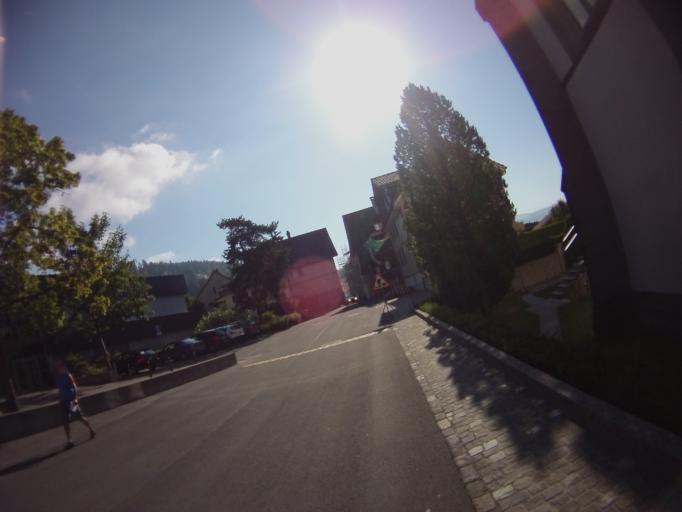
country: CH
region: Zug
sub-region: Zug
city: Unterageri
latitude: 47.1385
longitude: 8.5827
